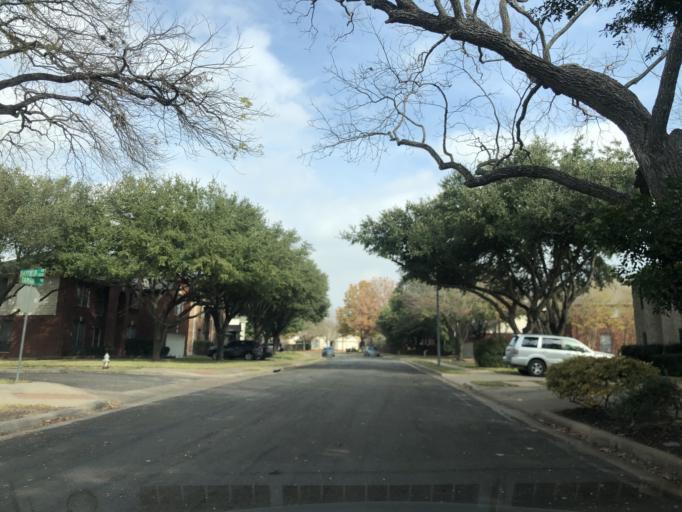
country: US
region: Texas
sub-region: Travis County
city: Wells Branch
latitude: 30.4179
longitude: -97.6797
